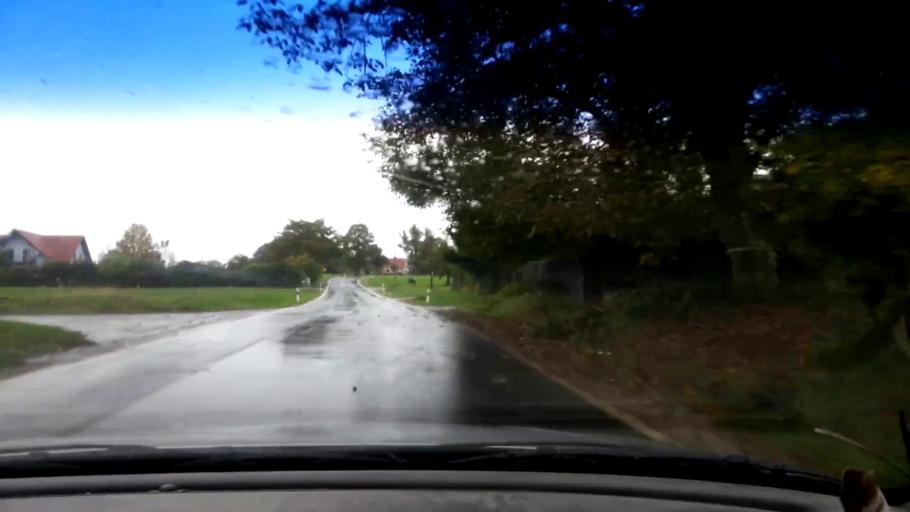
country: DE
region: Bavaria
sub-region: Upper Franconia
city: Poxdorf
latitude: 49.9381
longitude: 11.0798
